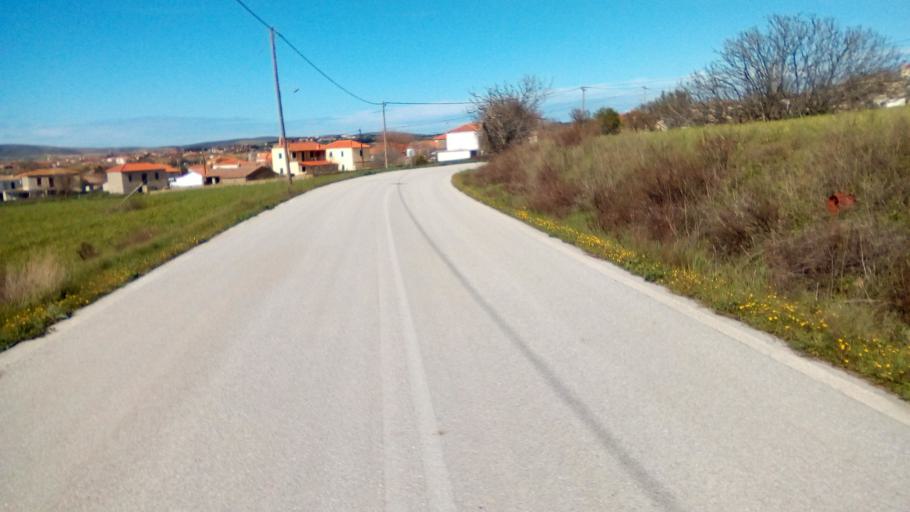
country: GR
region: North Aegean
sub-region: Nomos Lesvou
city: Myrina
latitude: 39.9318
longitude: 25.2310
